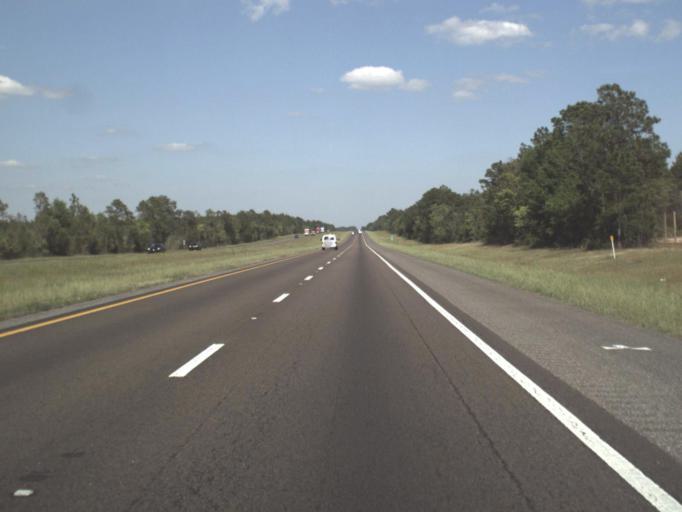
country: US
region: Florida
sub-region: Santa Rosa County
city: East Milton
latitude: 30.6740
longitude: -86.8338
